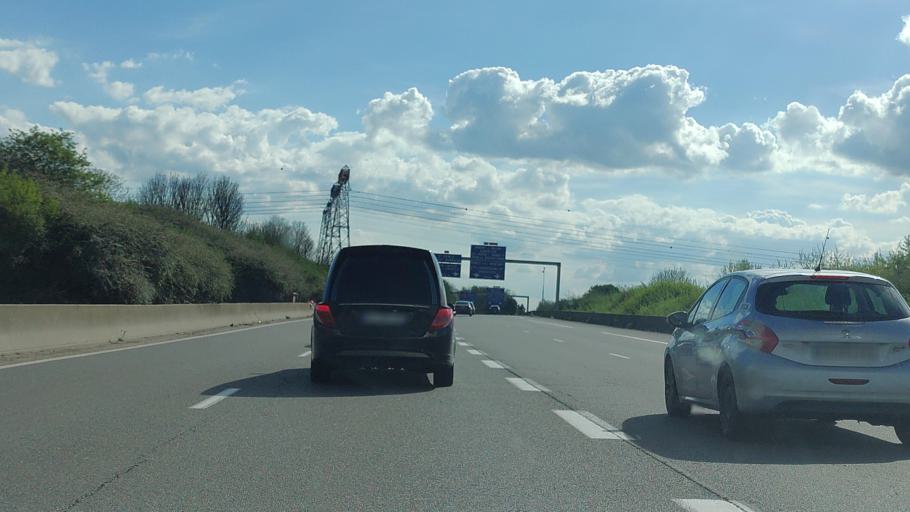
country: FR
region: Ile-de-France
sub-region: Departement du Val-d'Oise
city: Roissy-en-France
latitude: 48.9919
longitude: 2.5098
